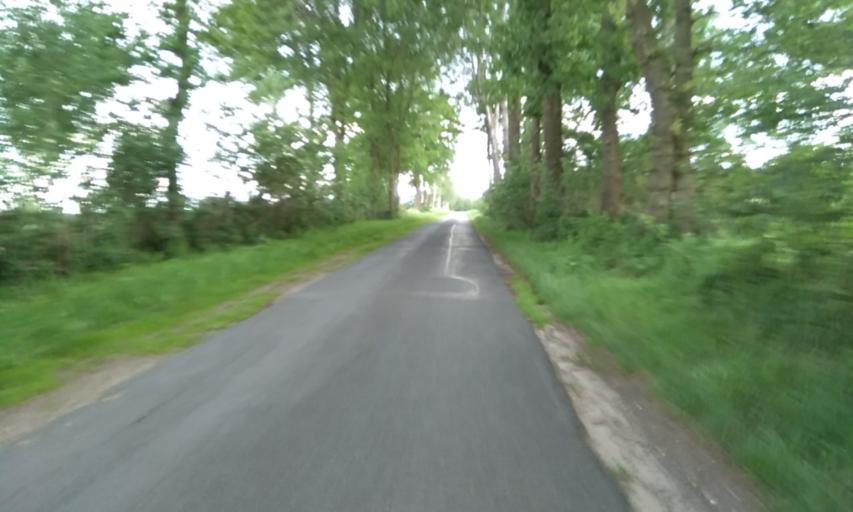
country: DE
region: Lower Saxony
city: Regesbostel
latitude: 53.3832
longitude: 9.6273
